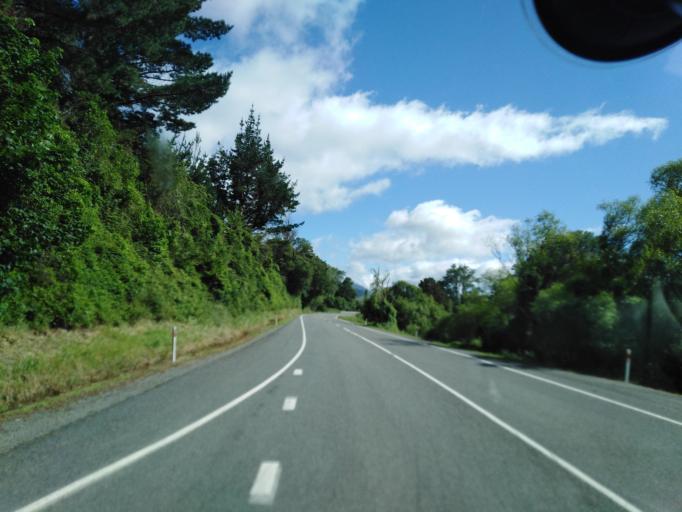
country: NZ
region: Nelson
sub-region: Nelson City
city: Nelson
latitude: -41.2521
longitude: 173.5775
